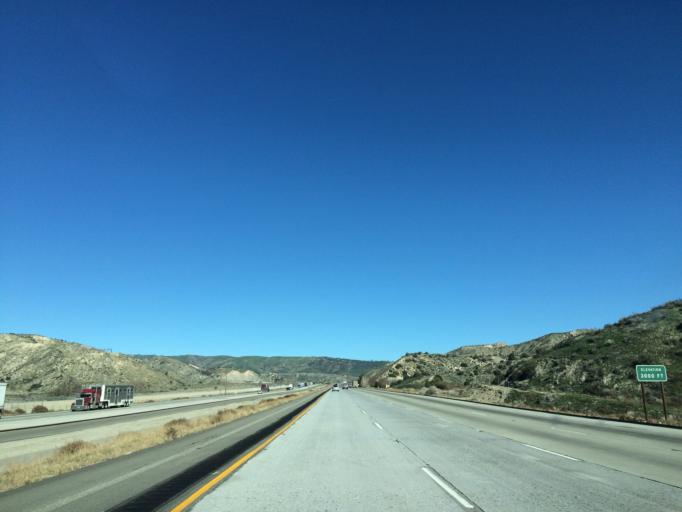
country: US
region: California
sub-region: Kern County
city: Lebec
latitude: 34.7294
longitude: -118.7984
